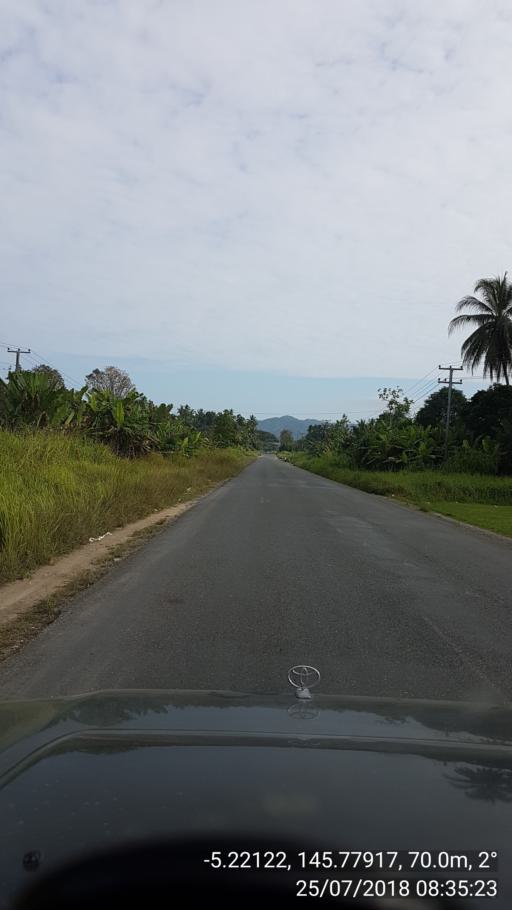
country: PG
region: Madang
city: Madang
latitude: -5.2211
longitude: 145.7792
